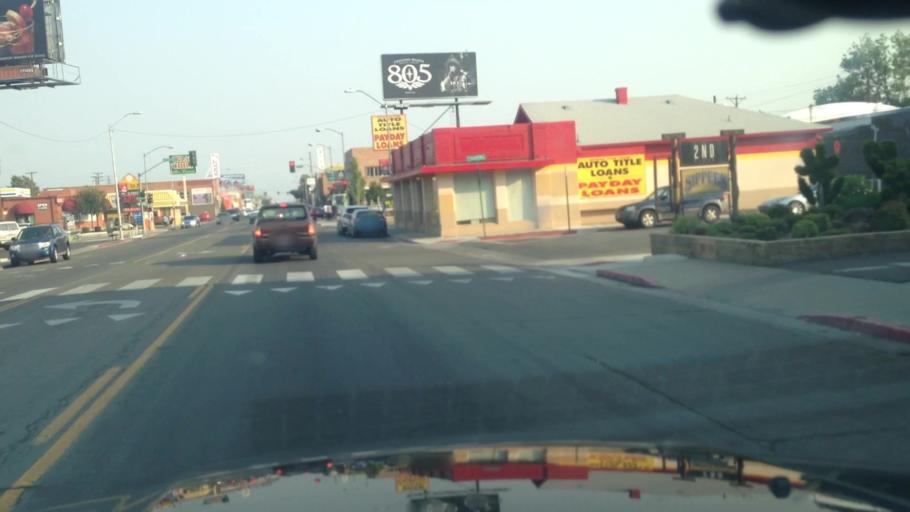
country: US
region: Nevada
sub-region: Washoe County
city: Reno
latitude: 39.5157
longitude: -119.8081
